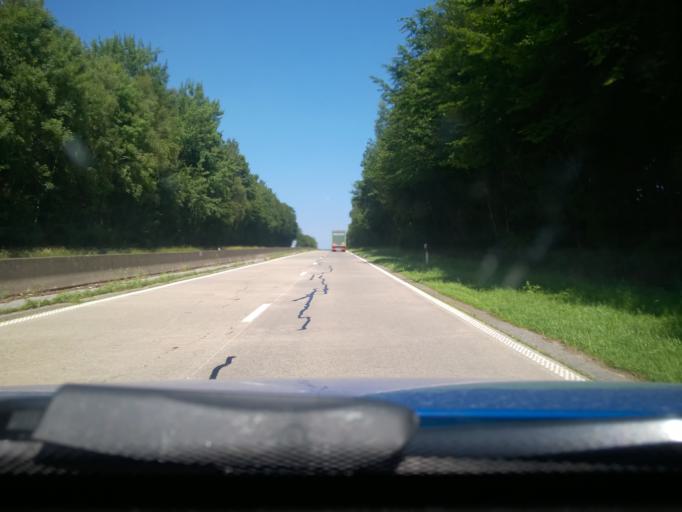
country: BE
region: Wallonia
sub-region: Province de Namur
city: Houyet
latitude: 50.2538
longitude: 5.0188
